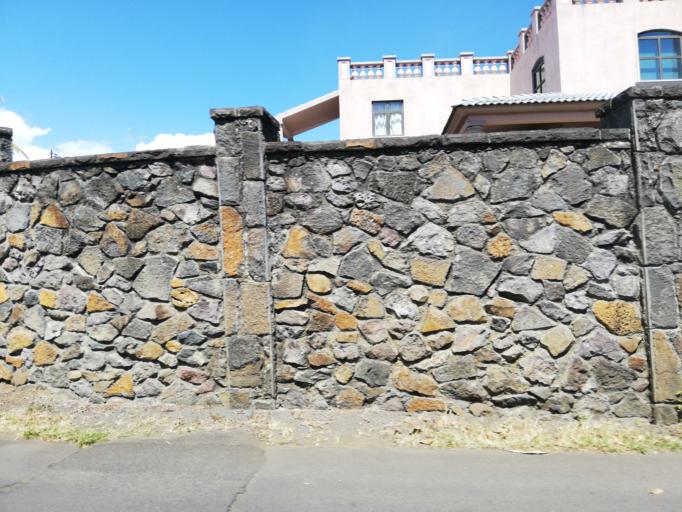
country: MU
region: Plaines Wilhems
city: Ebene
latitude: -20.2329
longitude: 57.4653
